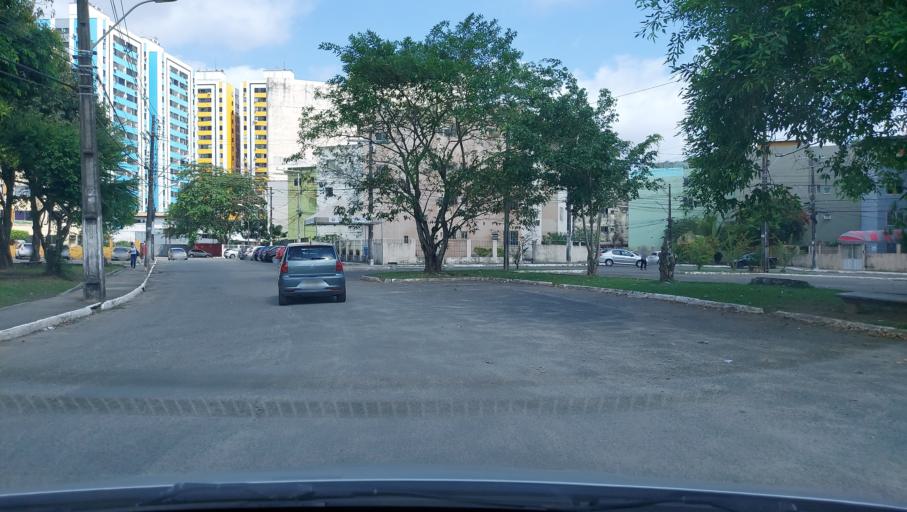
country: BR
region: Bahia
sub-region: Salvador
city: Salvador
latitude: -12.9626
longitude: -38.4300
